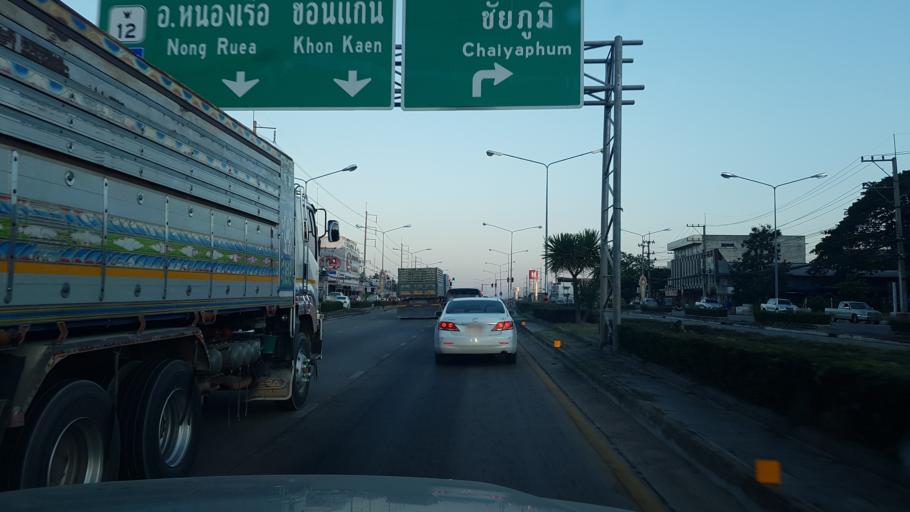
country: TH
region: Khon Kaen
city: Chum Phae
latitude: 16.5420
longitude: 102.1065
